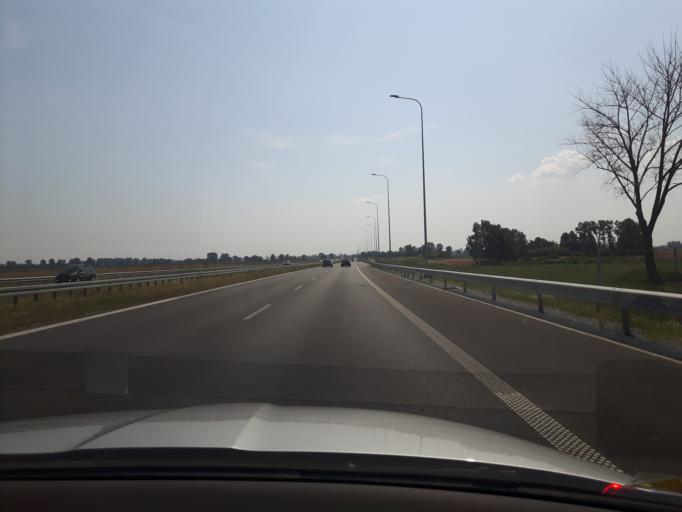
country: PL
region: Pomeranian Voivodeship
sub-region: Powiat nowodworski
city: Nowy Dwor Gdanski
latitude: 54.2327
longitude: 19.0431
